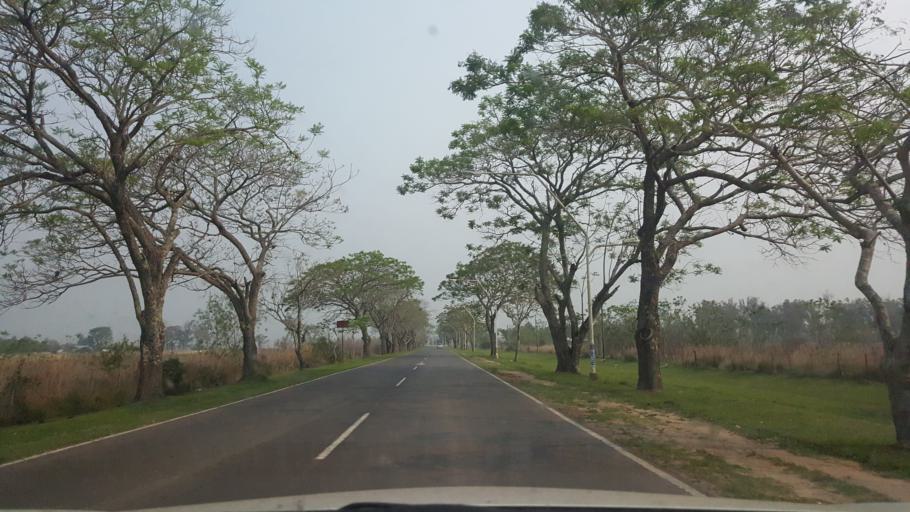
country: AR
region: Corrientes
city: Ita Ibate
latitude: -27.4377
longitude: -57.3397
